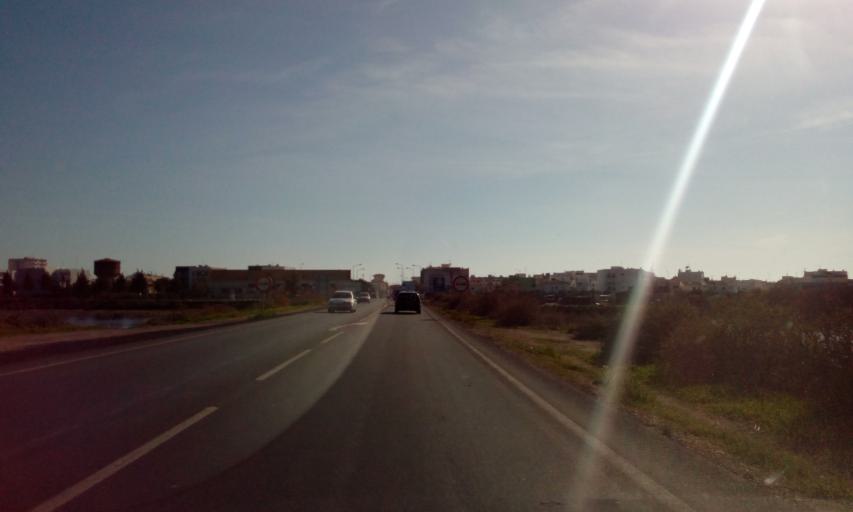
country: PT
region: Faro
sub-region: Vila Real de Santo Antonio
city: Vila Real de Santo Antonio
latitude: 37.1993
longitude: -7.4284
